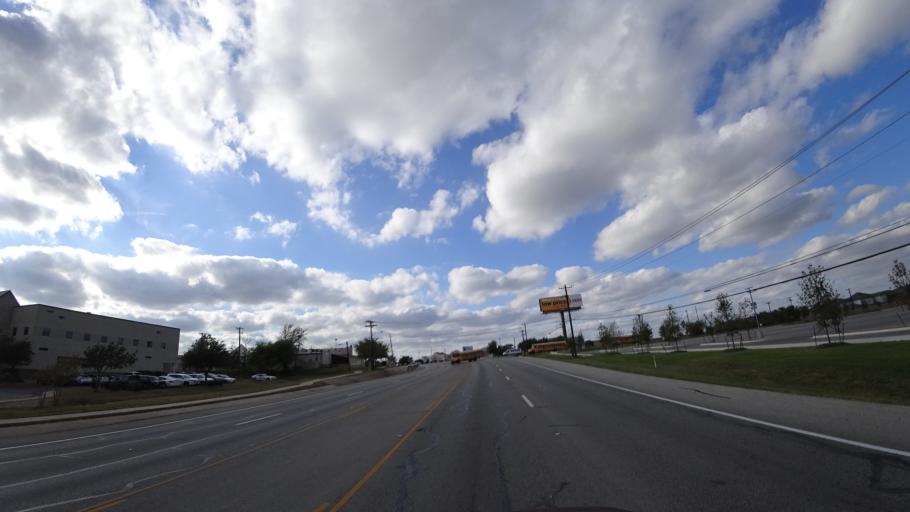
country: US
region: Texas
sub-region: Travis County
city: Pflugerville
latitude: 30.4469
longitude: -97.6357
